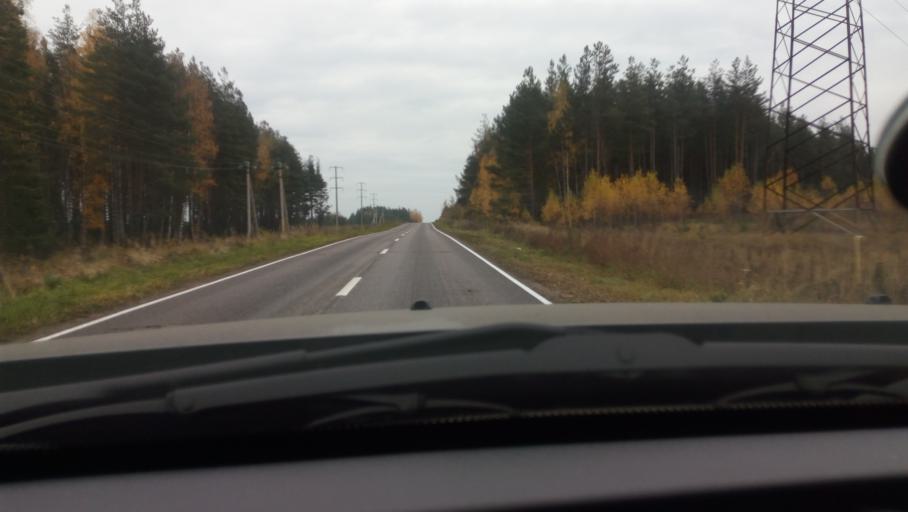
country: RU
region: Moskovskaya
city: Avsyunino
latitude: 55.5985
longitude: 39.2263
